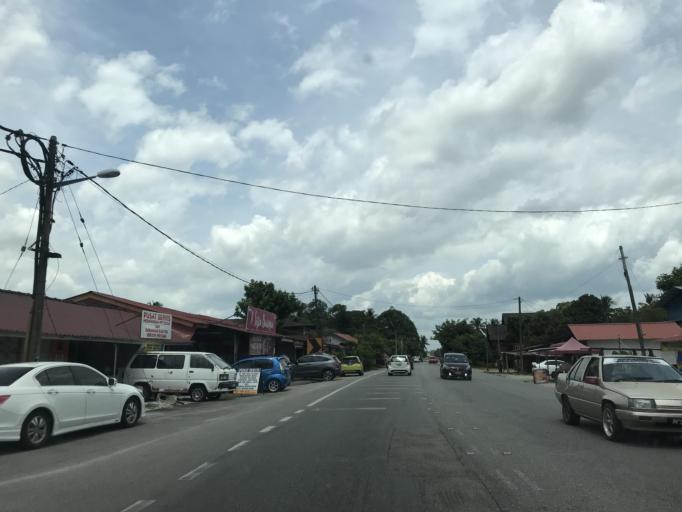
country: MY
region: Kelantan
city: Kota Bharu
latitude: 6.0752
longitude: 102.2086
